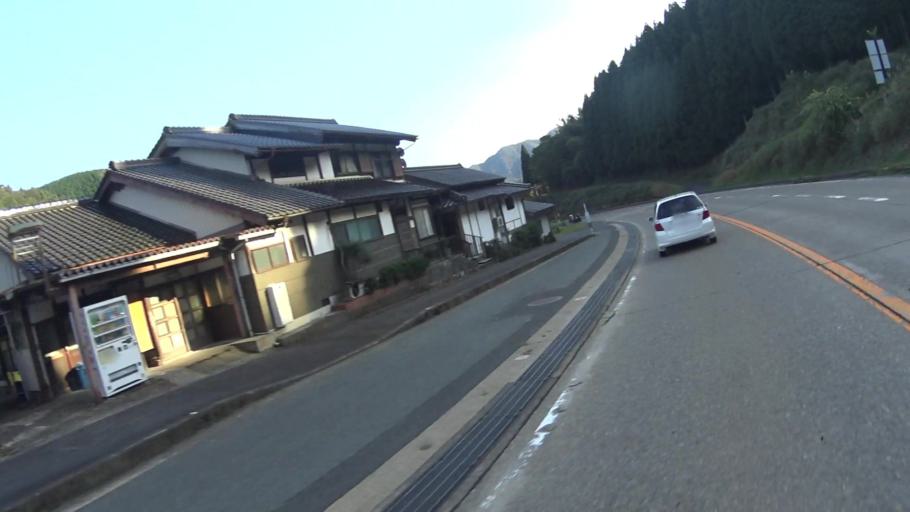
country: JP
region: Kyoto
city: Fukuchiyama
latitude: 35.4361
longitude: 135.0671
